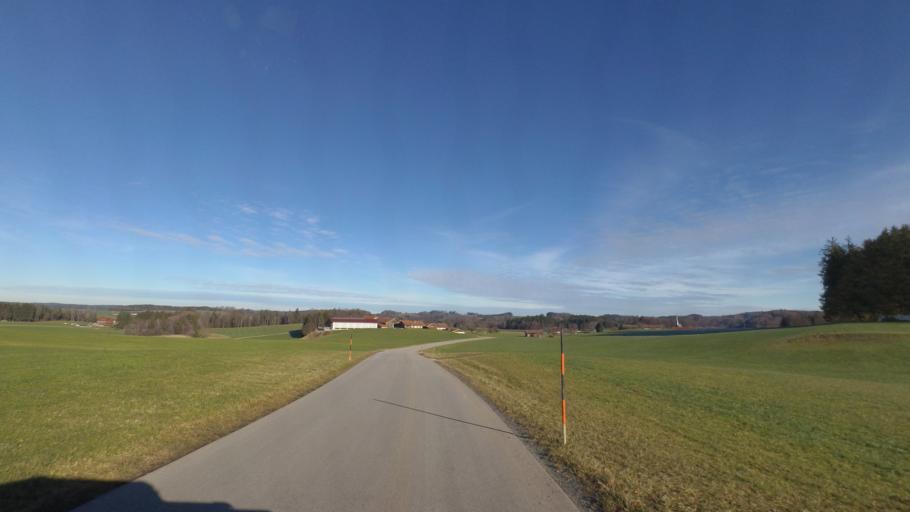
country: DE
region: Bavaria
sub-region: Upper Bavaria
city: Bergen
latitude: 47.8342
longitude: 12.5766
